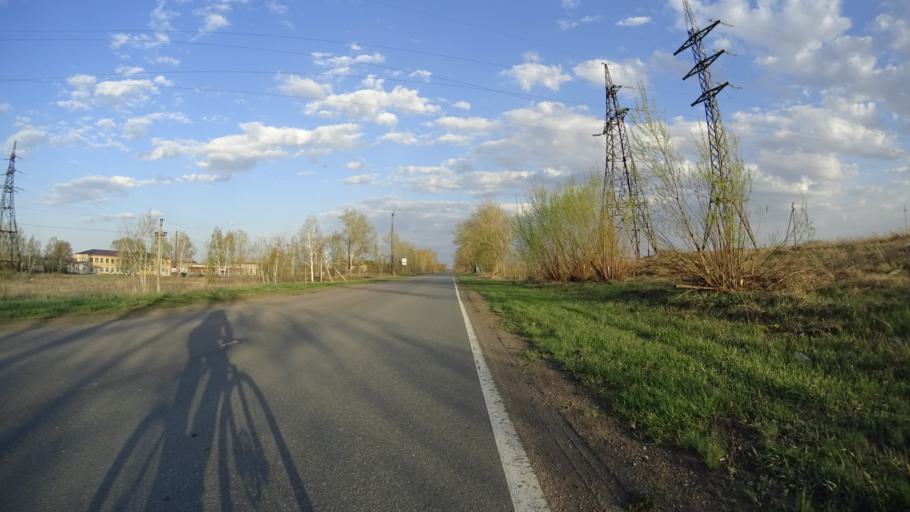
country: RU
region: Chelyabinsk
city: Troitsk
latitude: 54.0568
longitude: 61.5846
